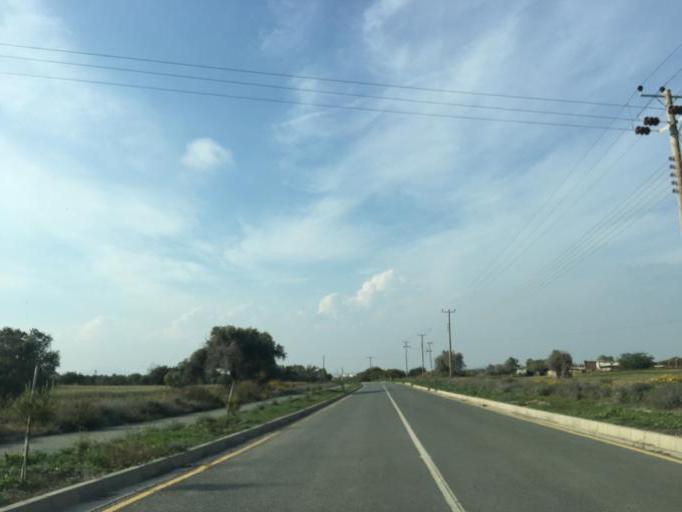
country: CY
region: Larnaka
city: Tersefanou
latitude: 34.7872
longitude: 33.4924
